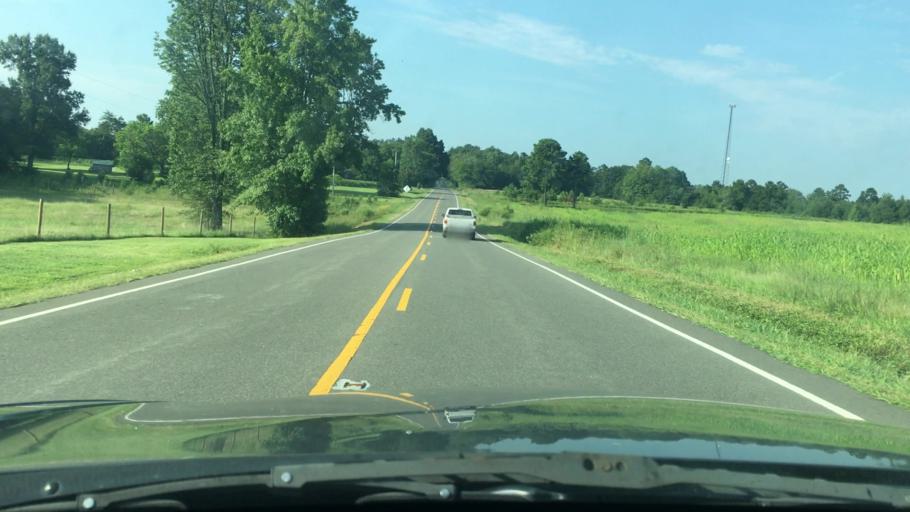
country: US
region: North Carolina
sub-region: Caswell County
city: Yanceyville
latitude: 36.3067
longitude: -79.3623
